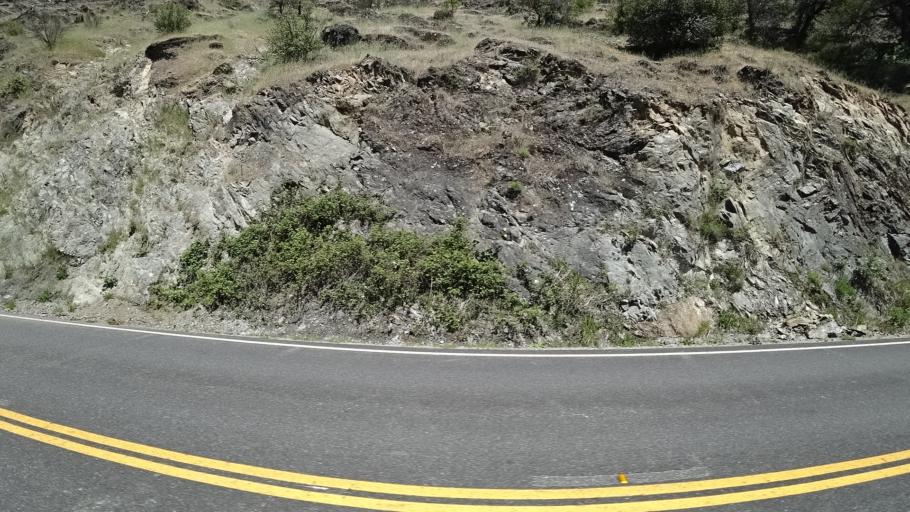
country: US
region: California
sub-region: Trinity County
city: Weaverville
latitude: 40.7358
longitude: -123.0558
